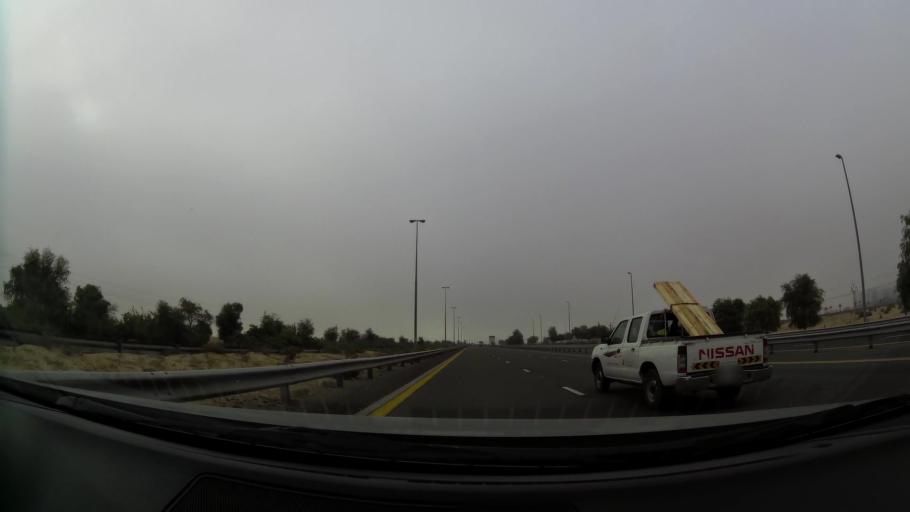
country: AE
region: Dubai
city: Dubai
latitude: 25.0530
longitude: 55.4240
